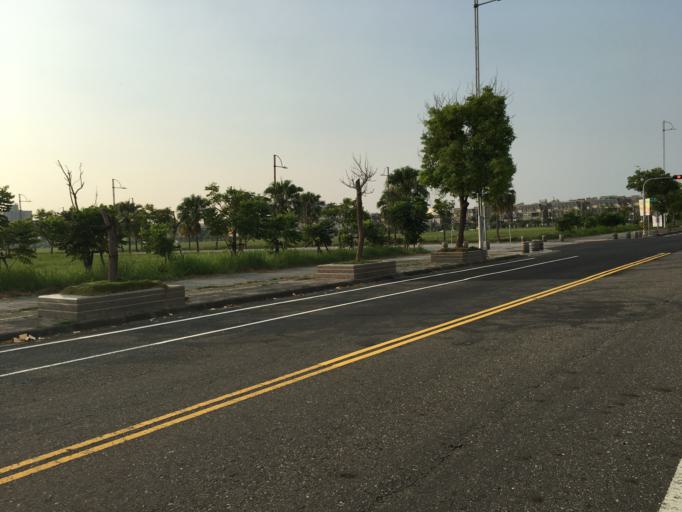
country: TW
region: Taiwan
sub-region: Chiayi
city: Taibao
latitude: 23.4615
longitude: 120.2996
